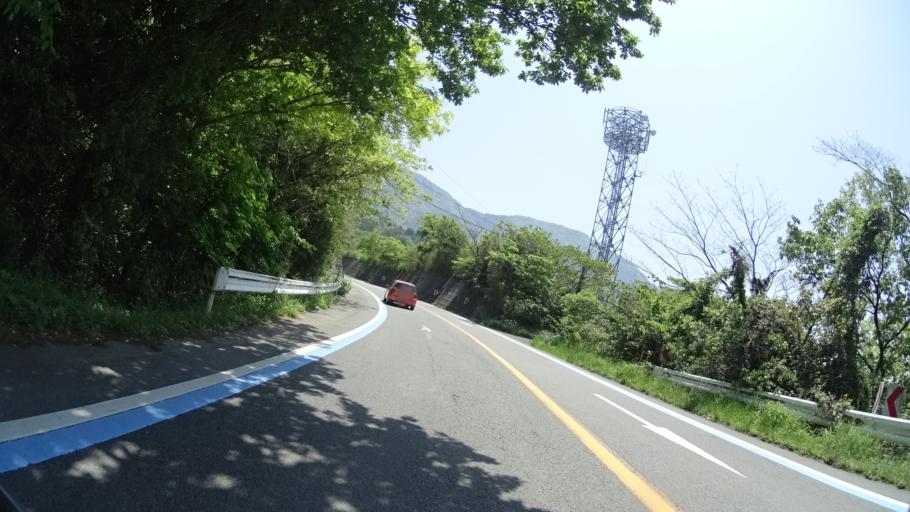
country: JP
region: Ehime
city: Iyo
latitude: 33.7122
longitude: 132.6681
